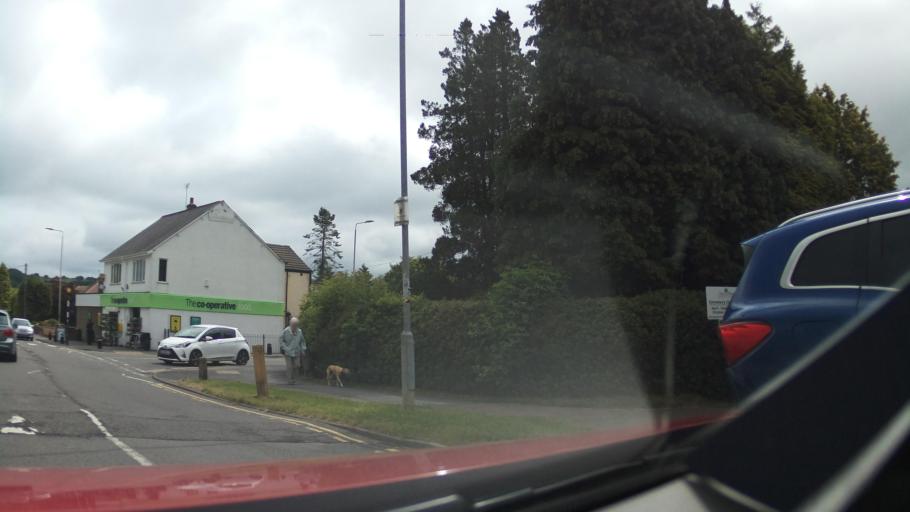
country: GB
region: England
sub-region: Leicestershire
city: Coalville
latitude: 52.7266
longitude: -1.3408
